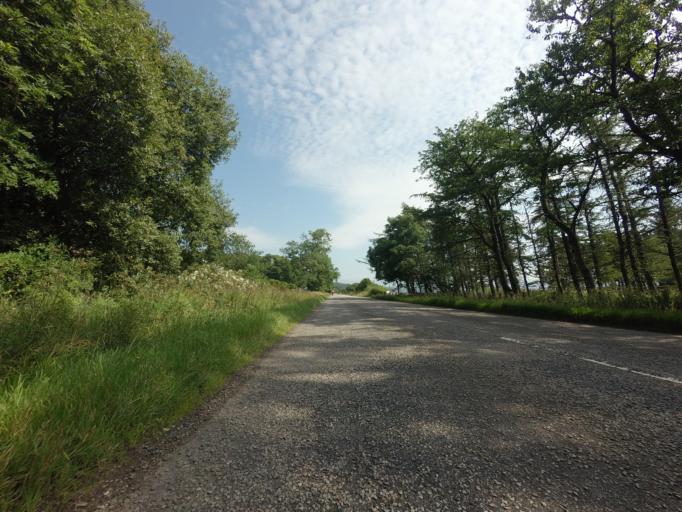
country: GB
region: Scotland
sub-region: Highland
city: Alness
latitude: 57.9144
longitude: -4.3836
